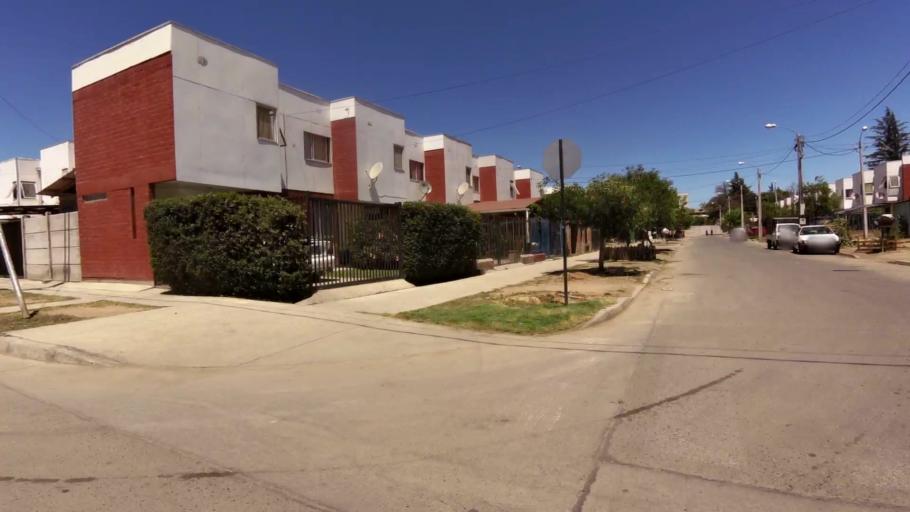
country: CL
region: O'Higgins
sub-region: Provincia de Cachapoal
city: Rancagua
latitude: -34.1642
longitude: -70.7557
